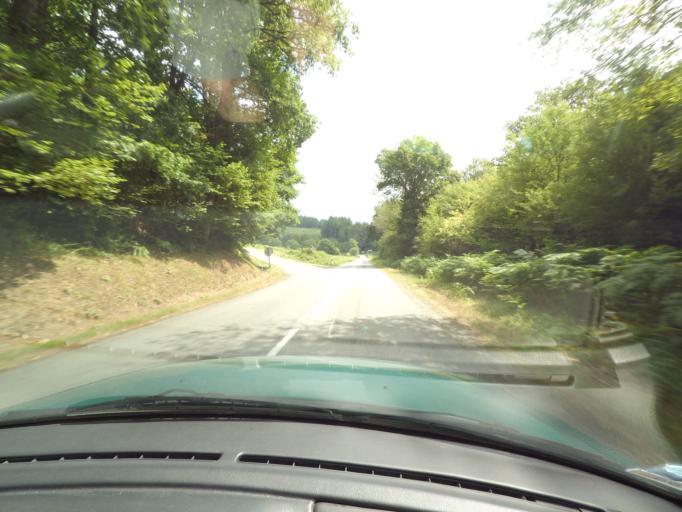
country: FR
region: Limousin
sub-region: Departement de la Haute-Vienne
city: Eymoutiers
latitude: 45.7139
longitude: 1.8515
